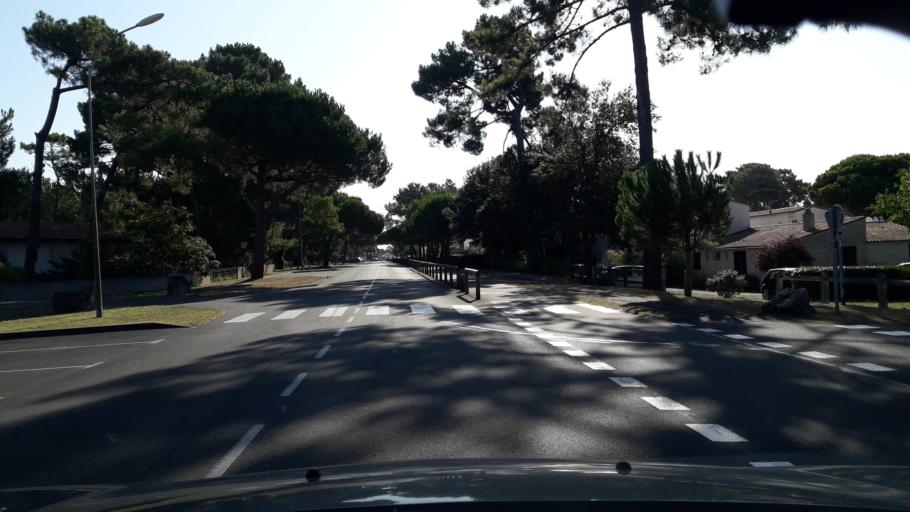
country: FR
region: Poitou-Charentes
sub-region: Departement de la Charente-Maritime
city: Les Mathes
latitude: 45.6895
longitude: -1.1858
